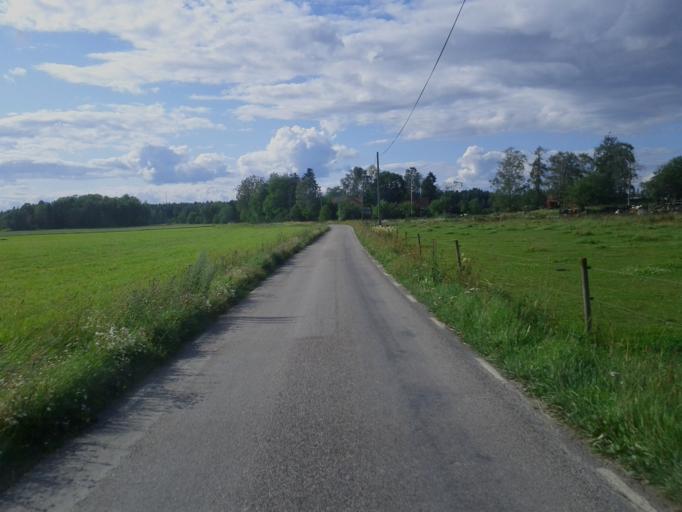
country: SE
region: Vaestmanland
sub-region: Sala Kommun
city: Sala
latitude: 59.9218
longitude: 16.5012
